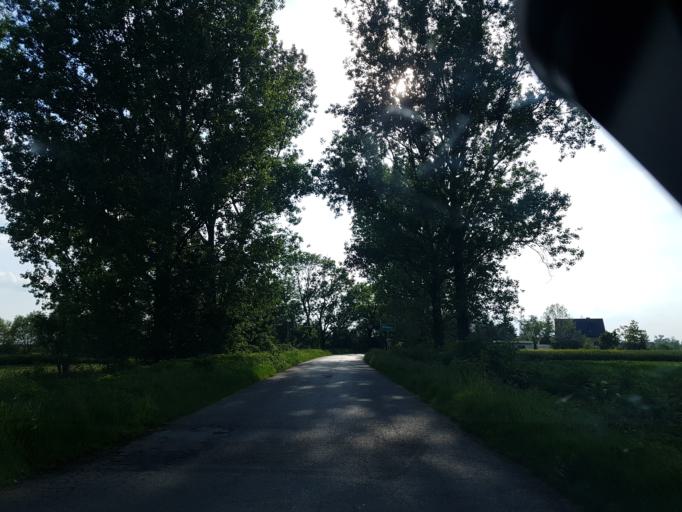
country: PL
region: Lower Silesian Voivodeship
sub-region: Powiat strzelinski
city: Wiazow
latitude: 50.8404
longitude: 17.2226
